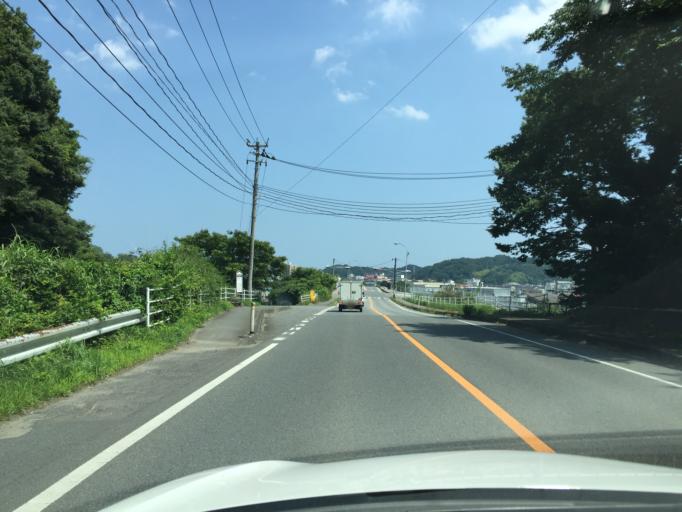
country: JP
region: Fukushima
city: Iwaki
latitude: 37.0556
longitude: 140.8752
